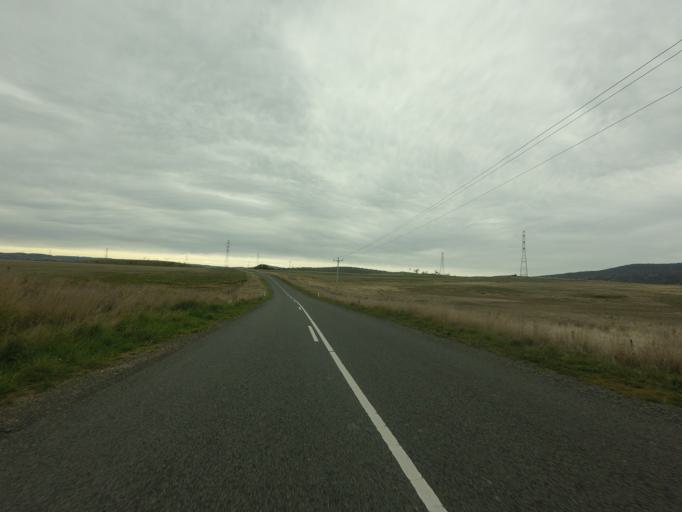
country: AU
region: Tasmania
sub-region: Derwent Valley
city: New Norfolk
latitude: -42.4222
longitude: 147.0007
